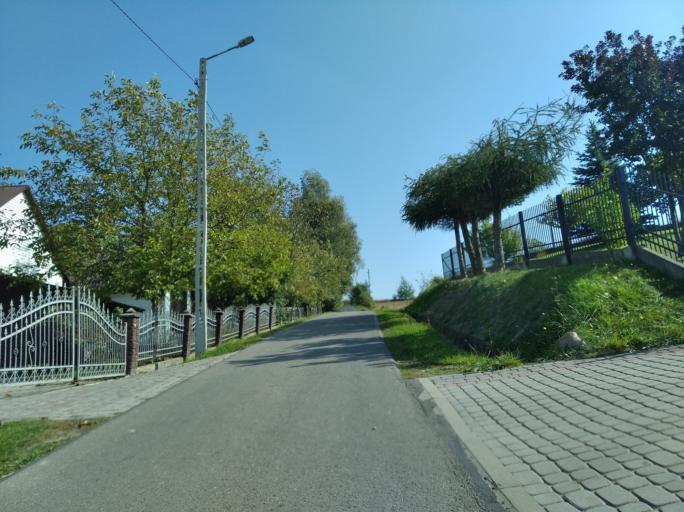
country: PL
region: Subcarpathian Voivodeship
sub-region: Powiat strzyzowski
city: Czudec
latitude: 49.9429
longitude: 21.8520
